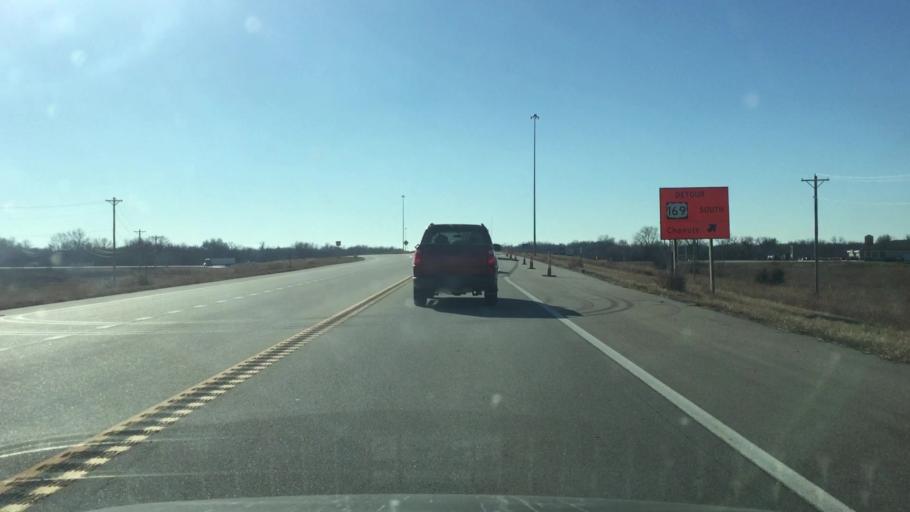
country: US
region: Kansas
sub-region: Allen County
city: Iola
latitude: 37.9267
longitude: -95.3796
